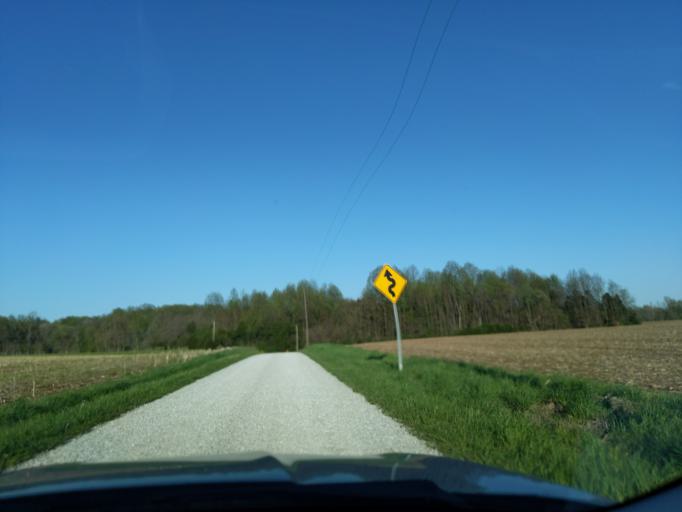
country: US
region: Indiana
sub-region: Decatur County
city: Westport
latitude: 39.1969
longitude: -85.4467
